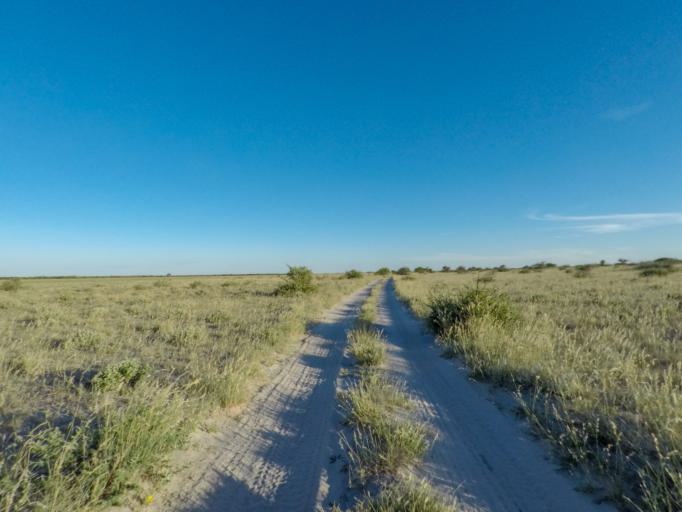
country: BW
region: Central
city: Rakops
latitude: -21.4029
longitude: 23.7958
